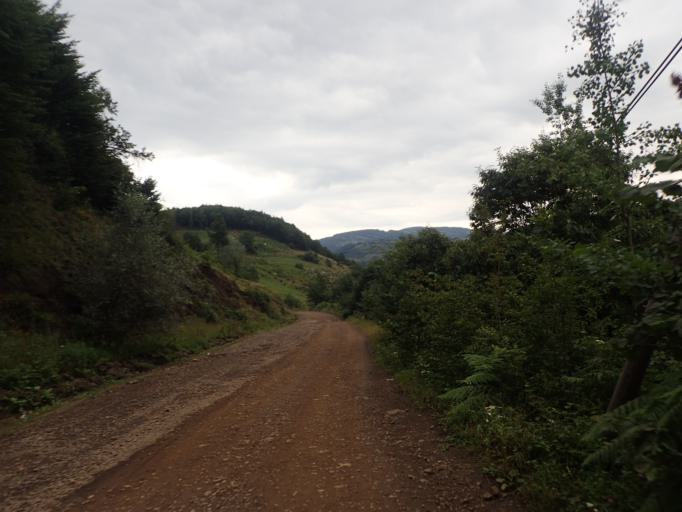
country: TR
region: Ordu
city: Akkus
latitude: 40.8168
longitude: 37.1044
